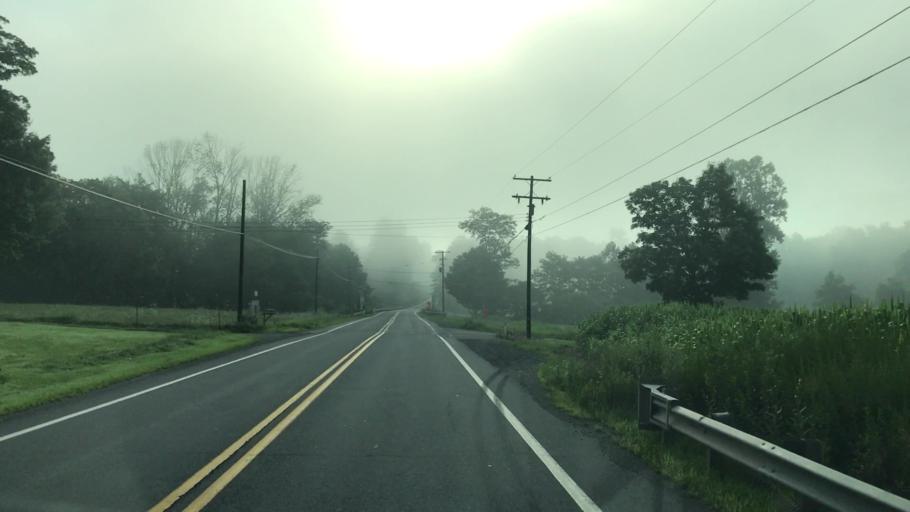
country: US
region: Pennsylvania
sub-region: Wyoming County
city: Factoryville
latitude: 41.6291
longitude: -75.7693
